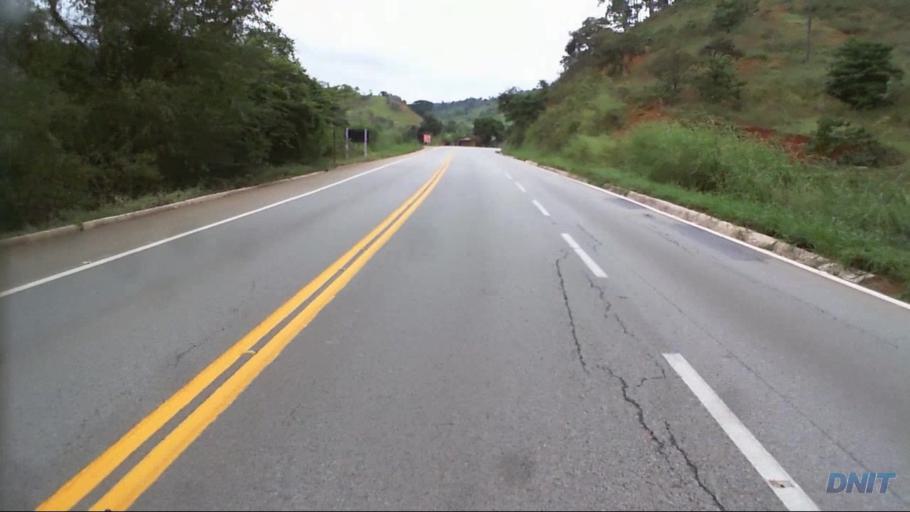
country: BR
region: Minas Gerais
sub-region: Nova Era
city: Nova Era
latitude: -19.7802
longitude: -43.0437
